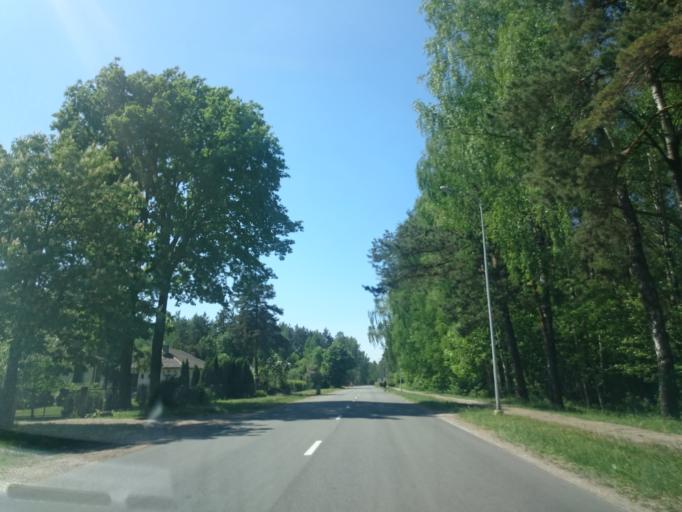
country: LV
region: Kekava
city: Balozi
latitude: 56.8719
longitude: 24.1127
